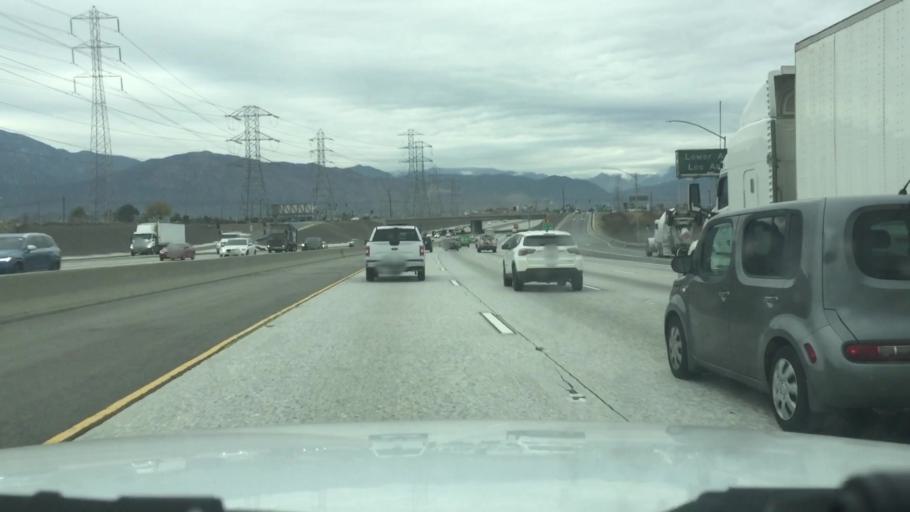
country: US
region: California
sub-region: Los Angeles County
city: Mayflower Village
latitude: 34.0887
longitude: -117.9943
